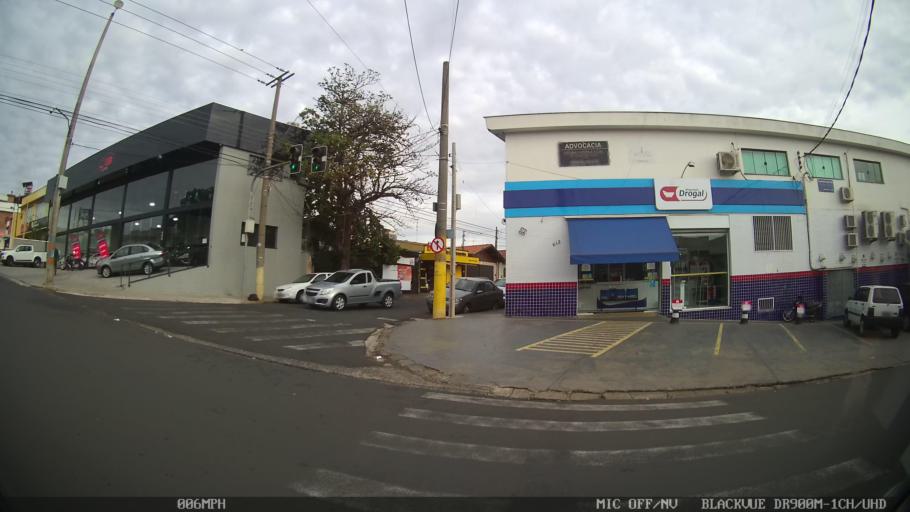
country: BR
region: Sao Paulo
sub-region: Piracicaba
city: Piracicaba
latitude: -22.7389
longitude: -47.6246
